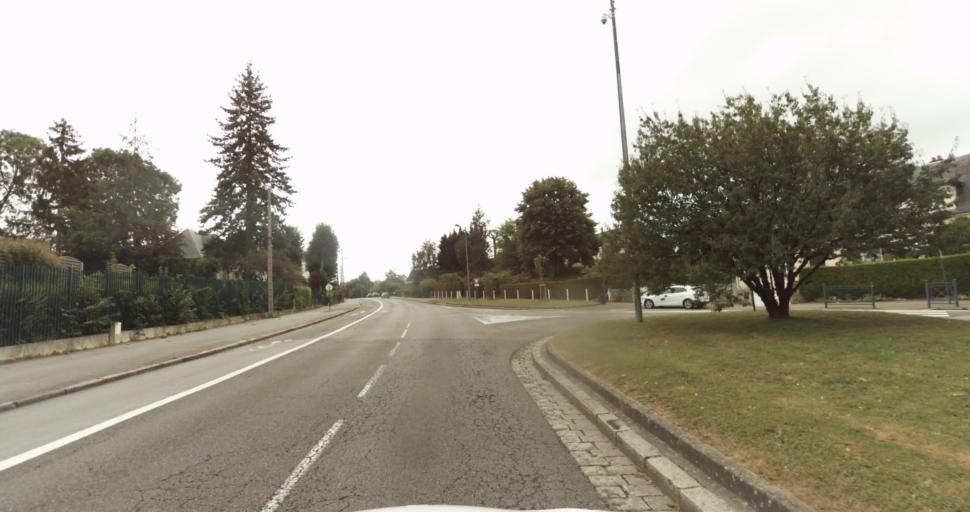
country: FR
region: Haute-Normandie
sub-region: Departement de l'Eure
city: Evreux
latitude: 49.0162
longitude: 1.1531
